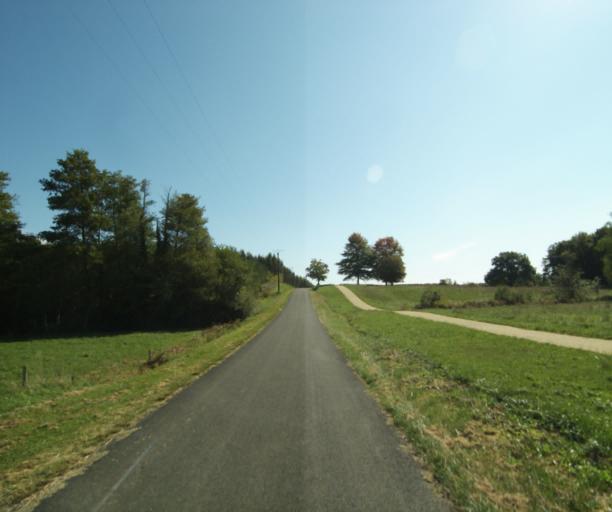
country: FR
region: Midi-Pyrenees
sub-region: Departement du Gers
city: Cazaubon
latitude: 43.9357
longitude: -0.0307
